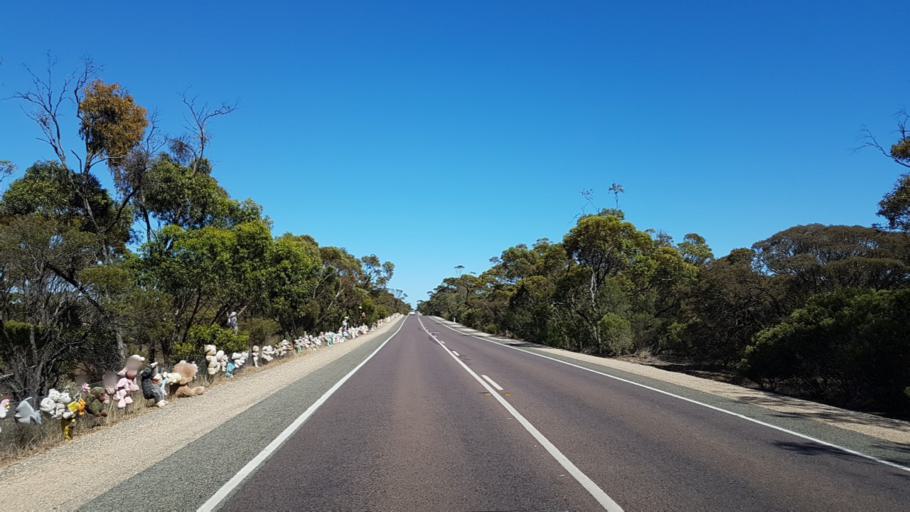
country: AU
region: South Australia
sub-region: Copper Coast
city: Kadina
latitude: -34.0495
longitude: 137.9730
